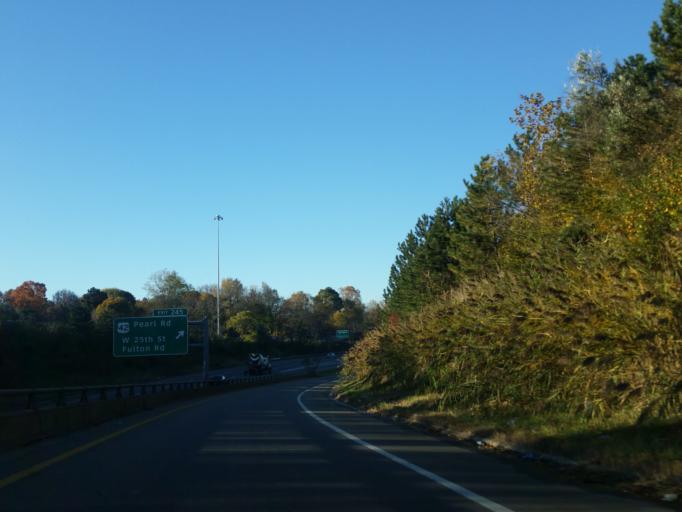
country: US
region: Ohio
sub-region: Cuyahoga County
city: Newburgh Heights
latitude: 41.4600
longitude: -81.6954
